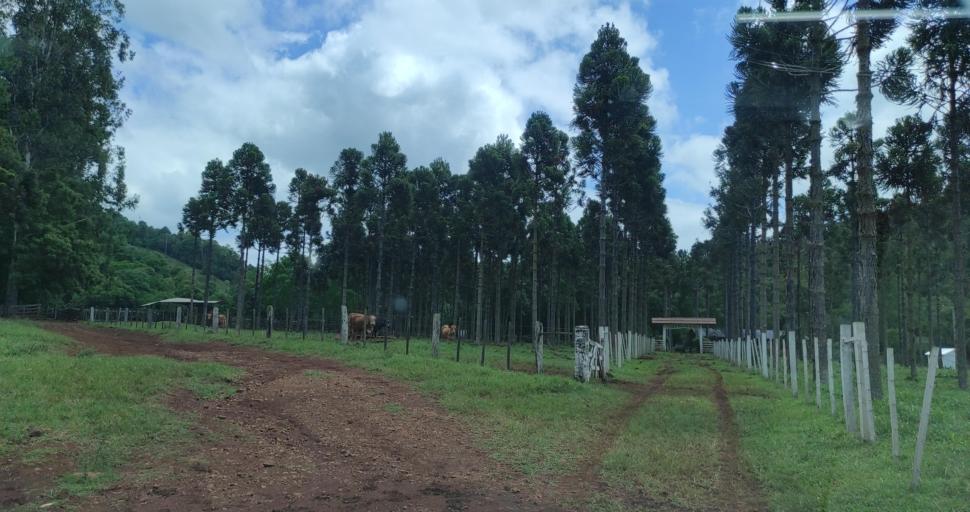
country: AR
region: Misiones
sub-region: Departamento de Veinticinco de Mayo
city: Veinticinco de Mayo
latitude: -27.4193
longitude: -54.7024
